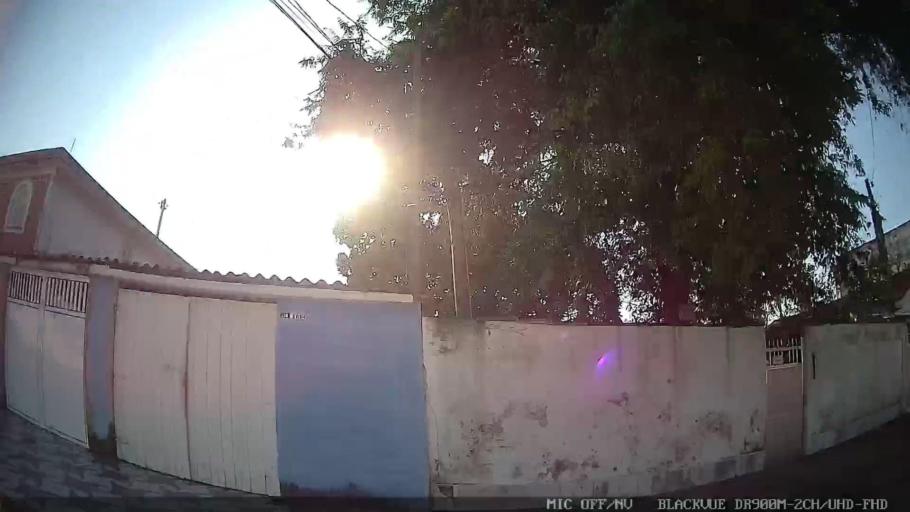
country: BR
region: Sao Paulo
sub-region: Guaruja
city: Guaruja
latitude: -23.9890
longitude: -46.2662
